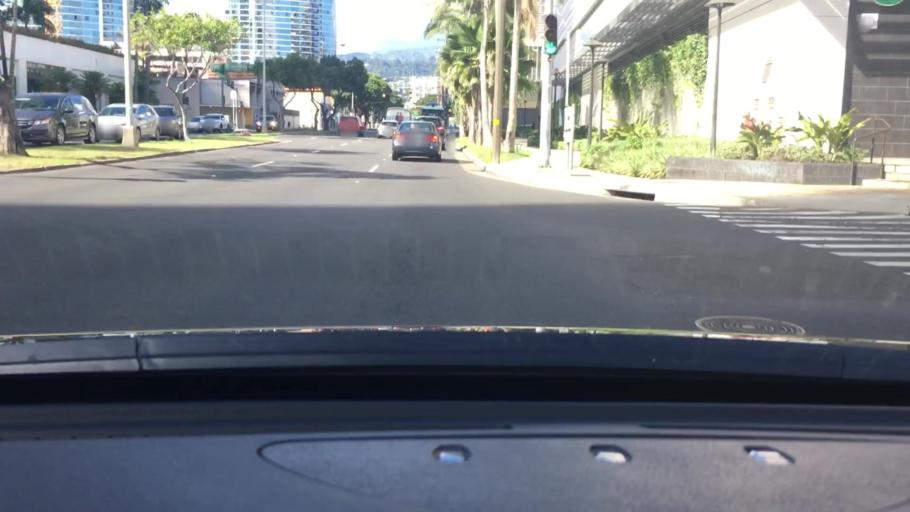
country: US
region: Hawaii
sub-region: Honolulu County
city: Honolulu
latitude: 21.2921
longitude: -157.8472
